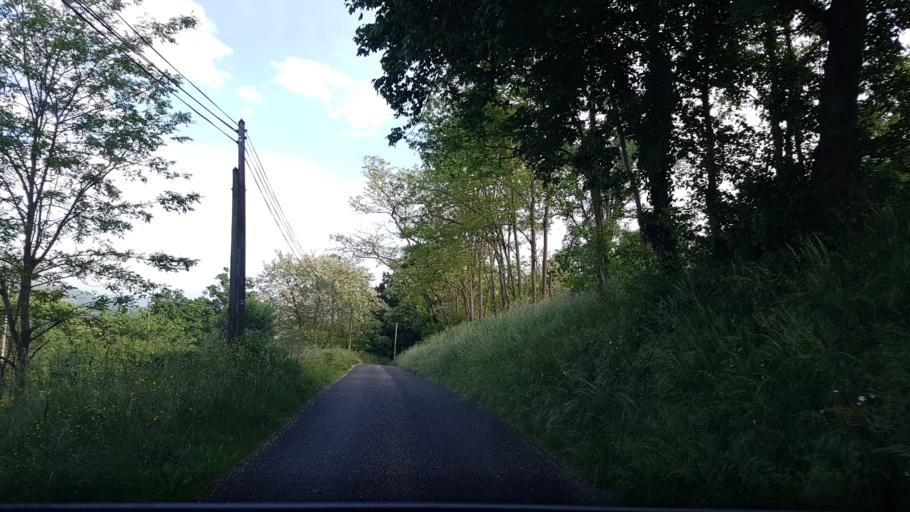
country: FR
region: Midi-Pyrenees
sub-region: Departement de l'Ariege
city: La Tour-du-Crieu
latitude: 43.1151
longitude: 1.7196
